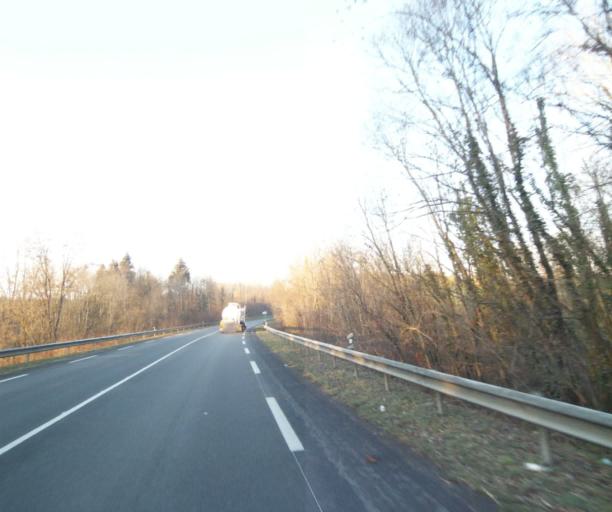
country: FR
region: Champagne-Ardenne
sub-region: Departement de la Haute-Marne
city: Bienville
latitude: 48.5663
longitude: 5.0355
